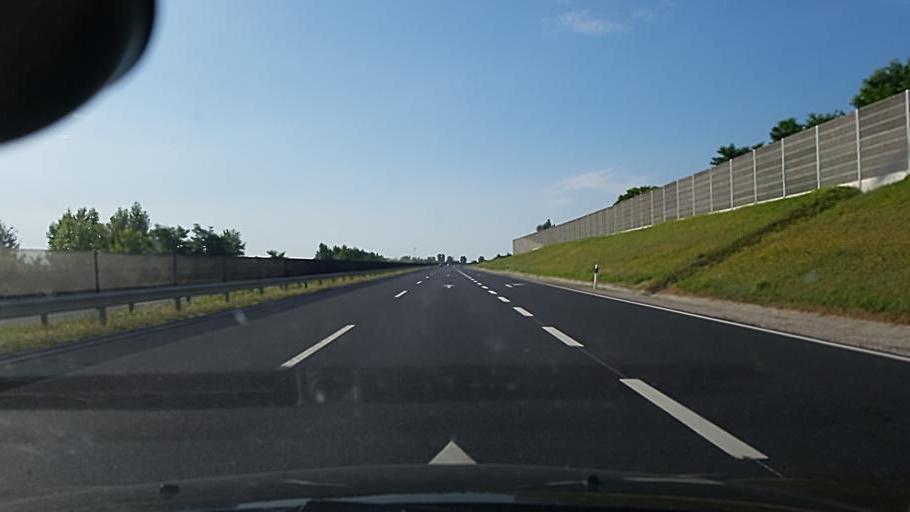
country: HU
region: Fejer
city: Racalmas
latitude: 47.0448
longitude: 18.8974
